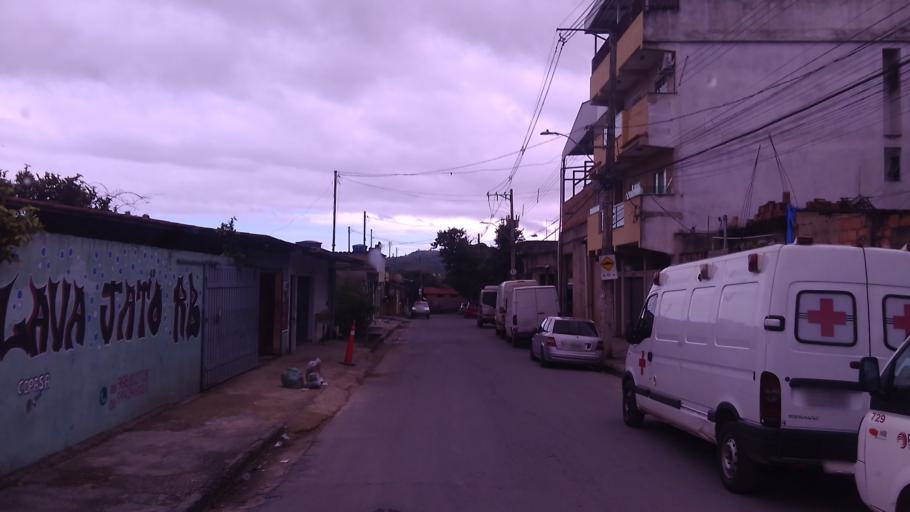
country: BR
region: Minas Gerais
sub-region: Santa Luzia
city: Santa Luzia
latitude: -19.8387
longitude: -43.9048
